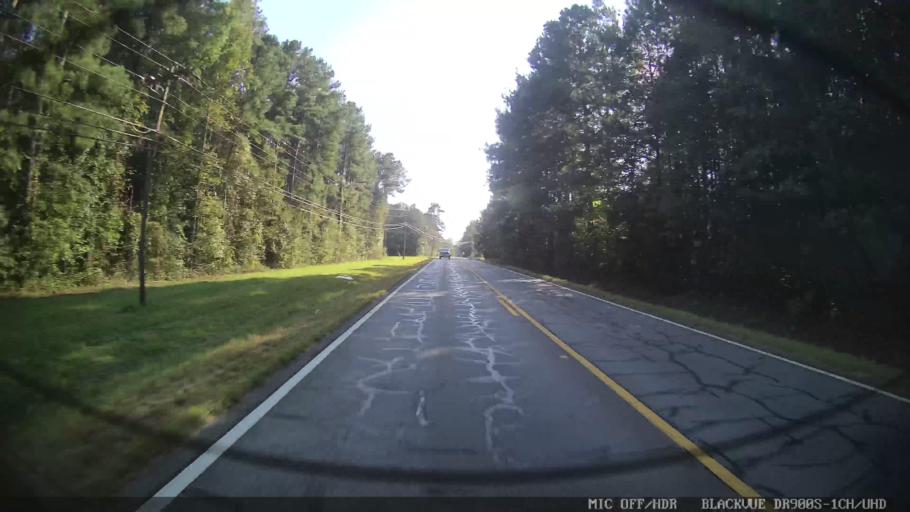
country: US
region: Georgia
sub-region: Murray County
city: Chatsworth
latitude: 34.6411
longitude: -84.8486
